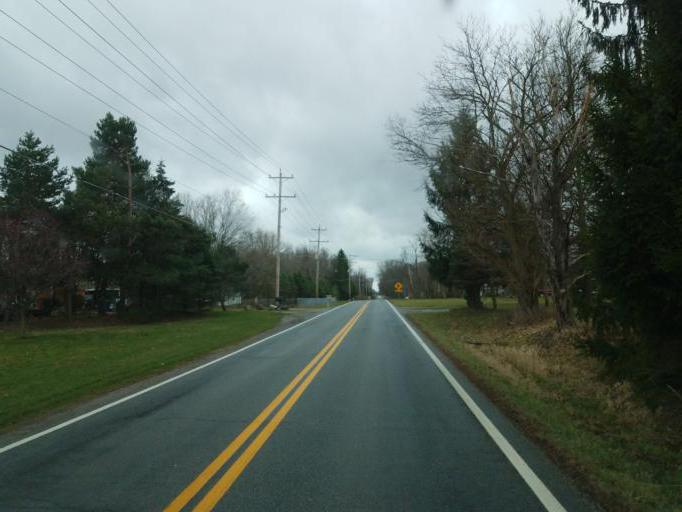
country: US
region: Ohio
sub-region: Delaware County
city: Sunbury
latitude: 40.2515
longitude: -82.9101
